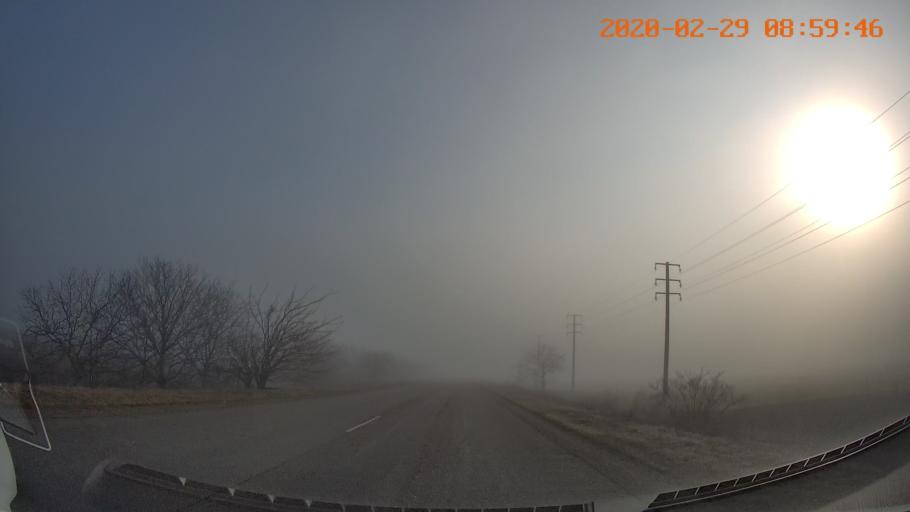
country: MD
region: Telenesti
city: Tiraspolul Nou
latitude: 46.9210
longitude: 29.6642
